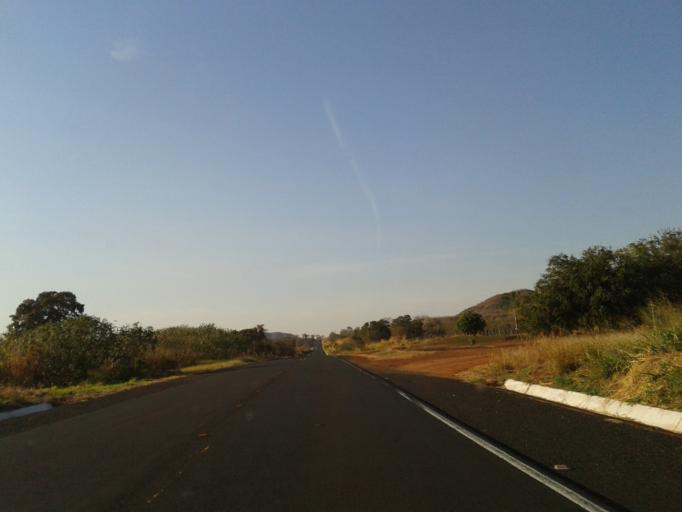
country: BR
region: Minas Gerais
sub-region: Santa Vitoria
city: Santa Vitoria
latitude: -19.1796
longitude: -50.0420
